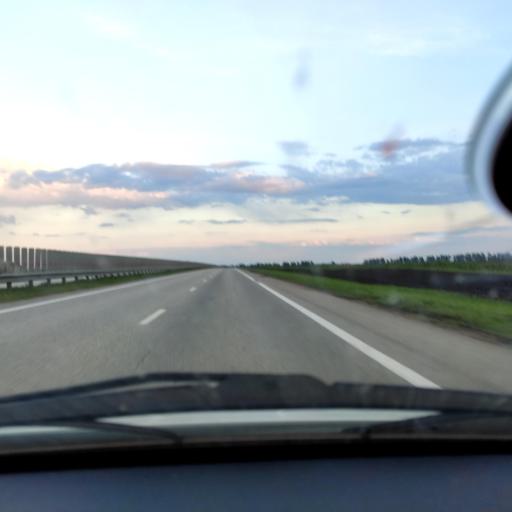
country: RU
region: Bashkortostan
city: Kushnarenkovo
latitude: 55.0958
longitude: 55.2460
